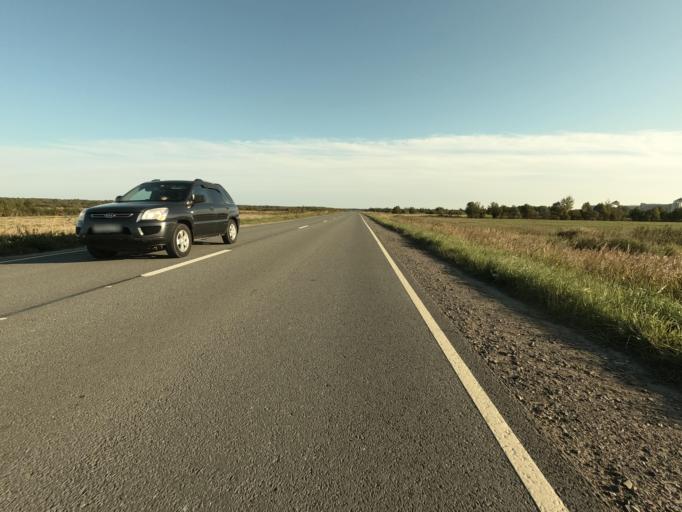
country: RU
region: St.-Petersburg
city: Sapernyy
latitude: 59.7514
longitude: 30.6369
